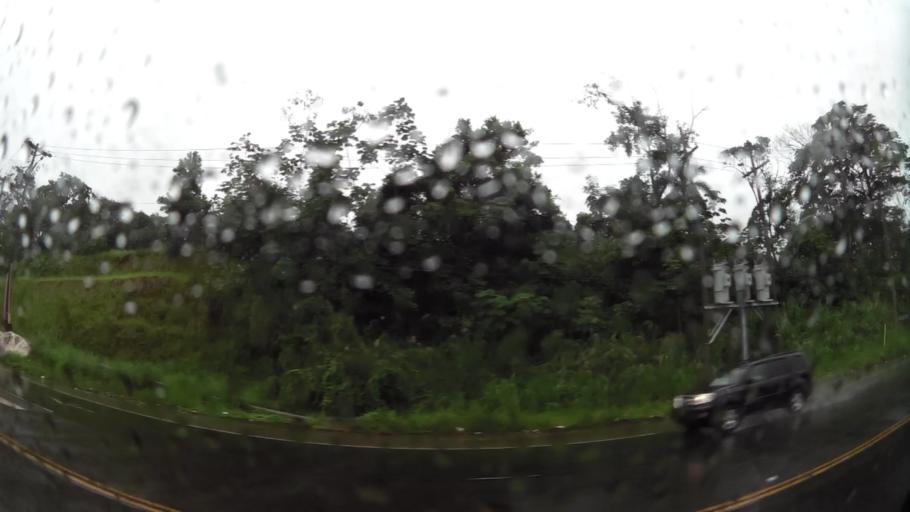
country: PA
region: Colon
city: Santa Rita Arriba
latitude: 9.3313
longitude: -79.8027
